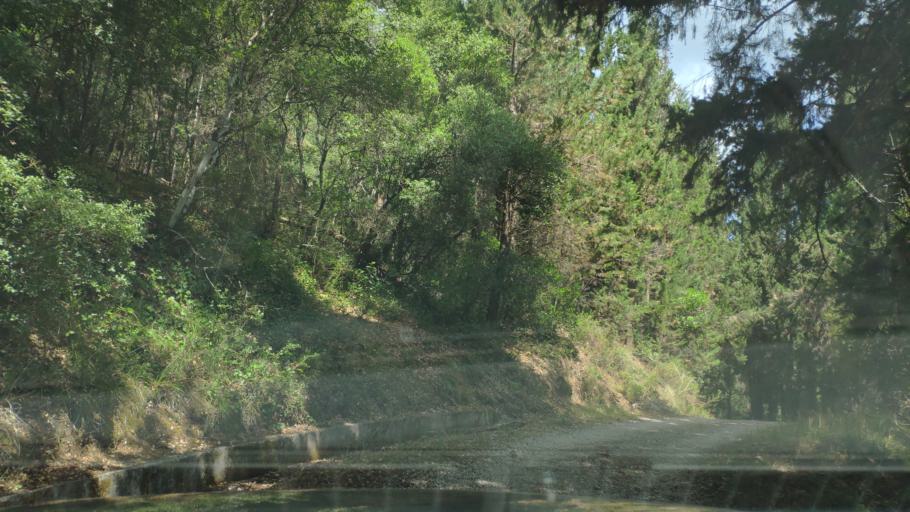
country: GR
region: Ionian Islands
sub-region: Lefkada
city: Lefkada
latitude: 38.7986
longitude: 20.6728
